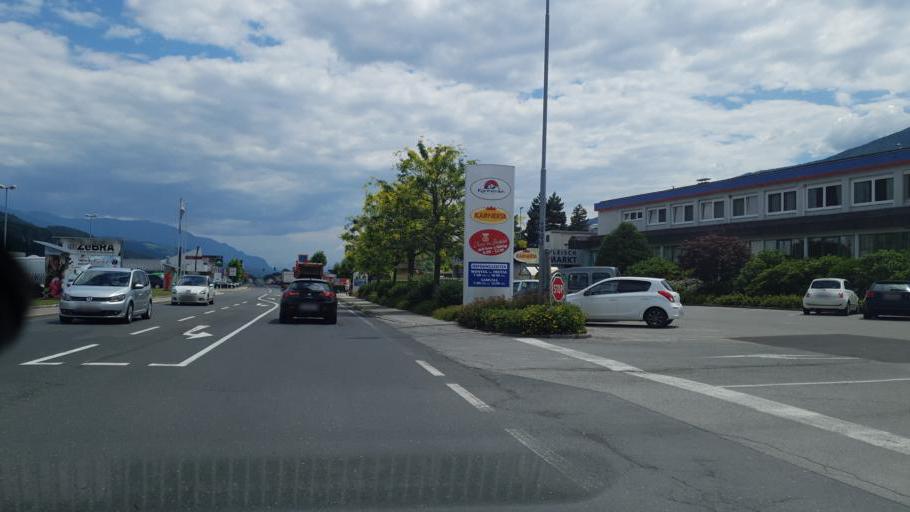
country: AT
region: Carinthia
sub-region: Politischer Bezirk Spittal an der Drau
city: Spittal an der Drau
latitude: 46.7900
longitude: 13.5157
